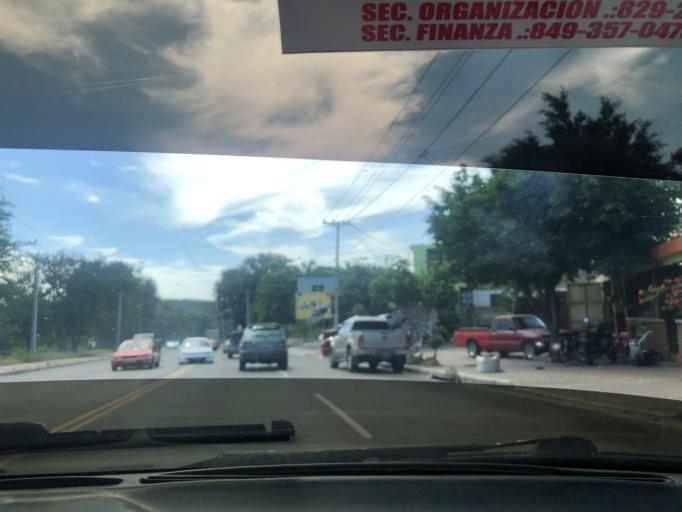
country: DO
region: Santiago
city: Santiago de los Caballeros
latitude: 19.4388
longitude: -70.6997
